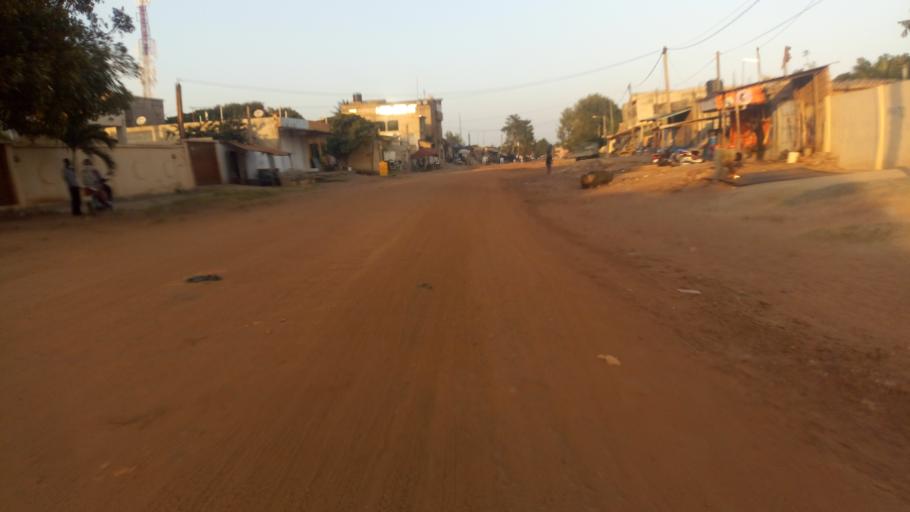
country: TG
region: Maritime
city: Lome
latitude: 6.1927
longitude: 1.1941
